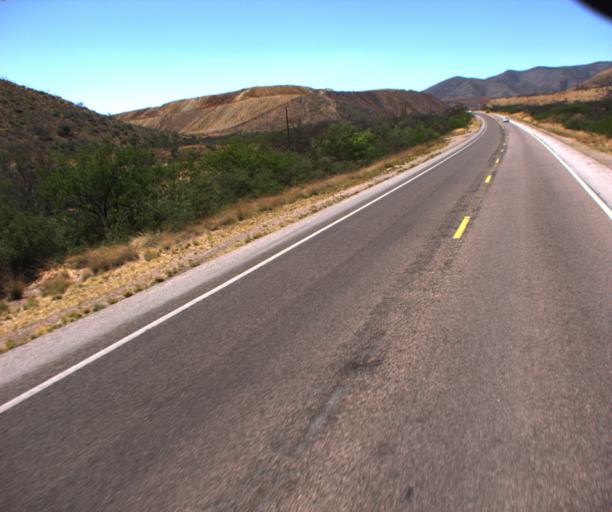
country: US
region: Arizona
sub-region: Cochise County
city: Bisbee
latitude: 31.4310
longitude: -109.8590
